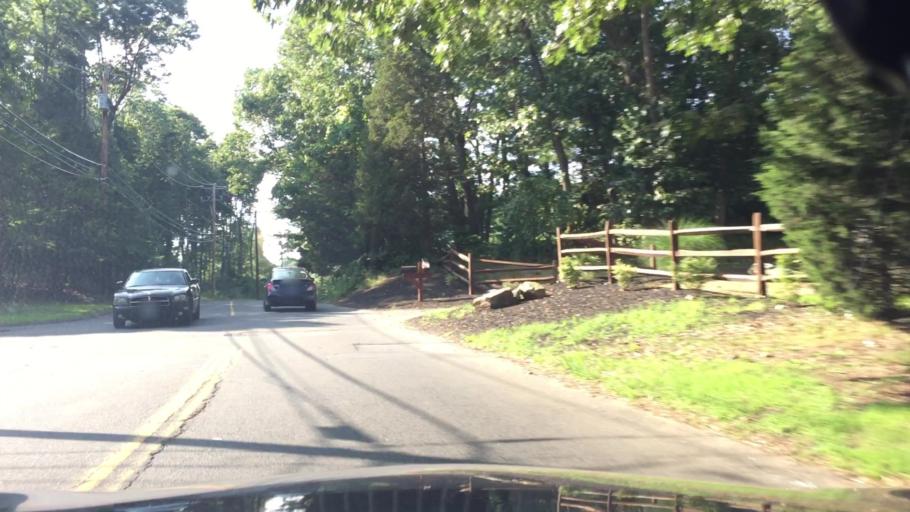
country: US
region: Connecticut
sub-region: New Haven County
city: Orange
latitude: 41.2497
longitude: -73.0156
